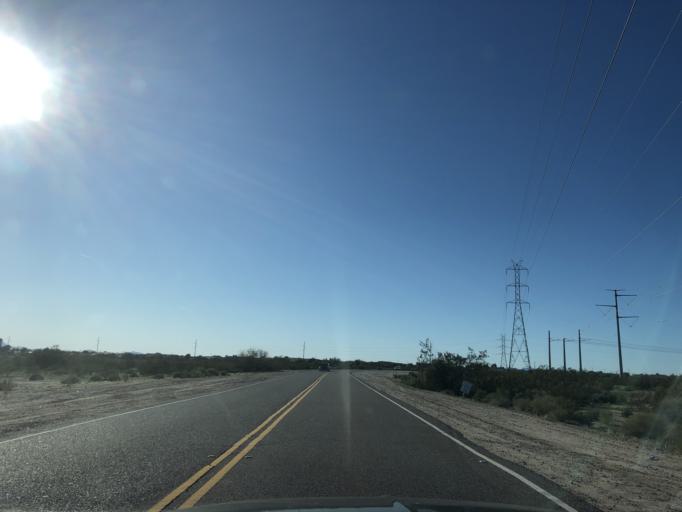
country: US
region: Arizona
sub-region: Maricopa County
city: Buckeye
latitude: 33.4207
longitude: -112.5937
